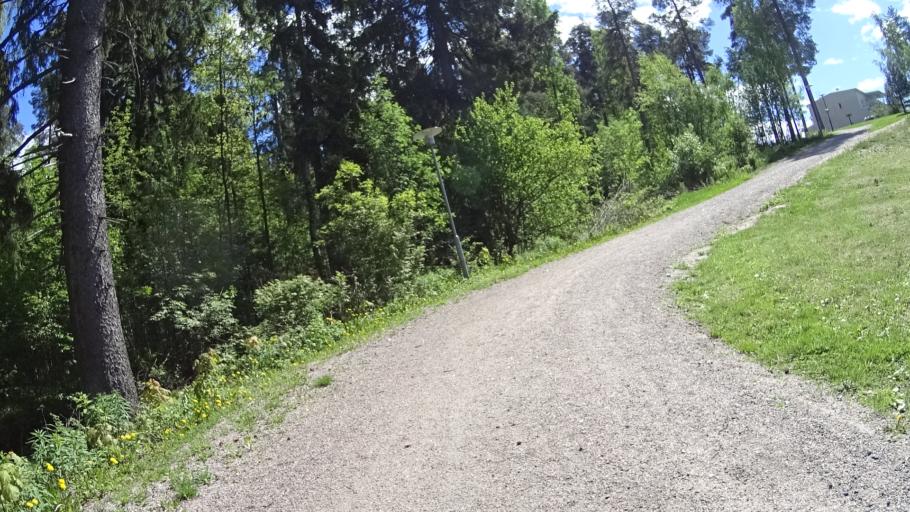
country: FI
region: Uusimaa
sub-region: Helsinki
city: Kauniainen
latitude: 60.2230
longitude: 24.6929
